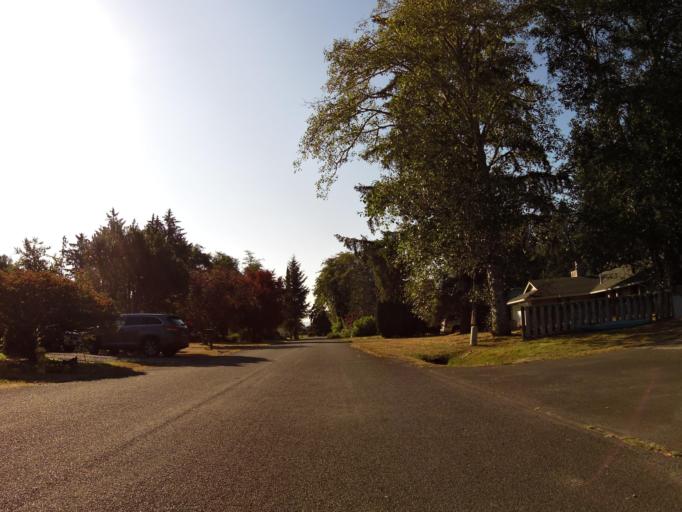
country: US
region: Oregon
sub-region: Clatsop County
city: Warrenton
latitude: 46.1368
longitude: -123.9345
